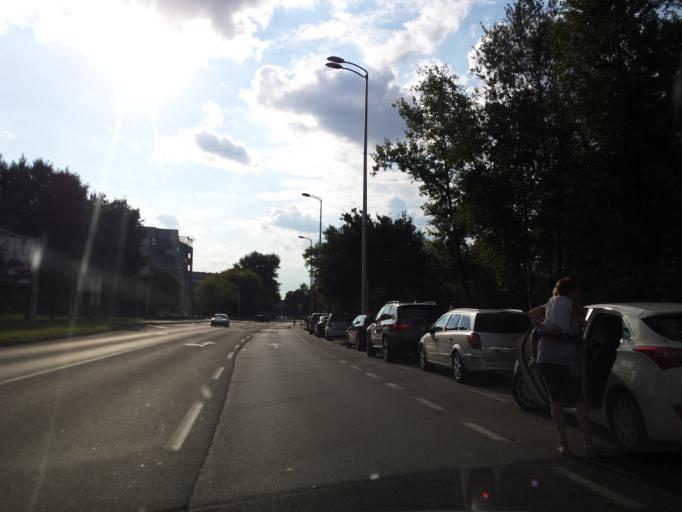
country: HR
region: Grad Zagreb
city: Novi Zagreb
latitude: 45.7828
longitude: 15.9878
